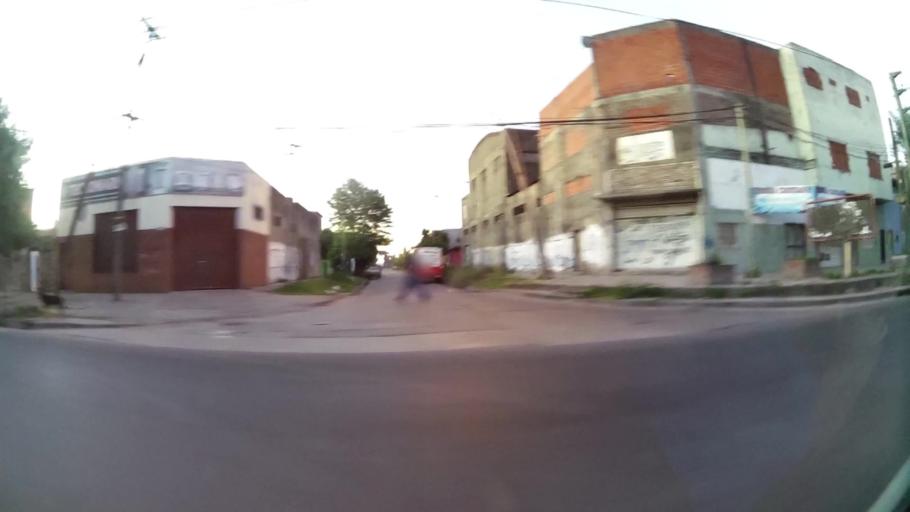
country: AR
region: Buenos Aires
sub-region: Partido de Moron
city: Moron
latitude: -34.7030
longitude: -58.6136
